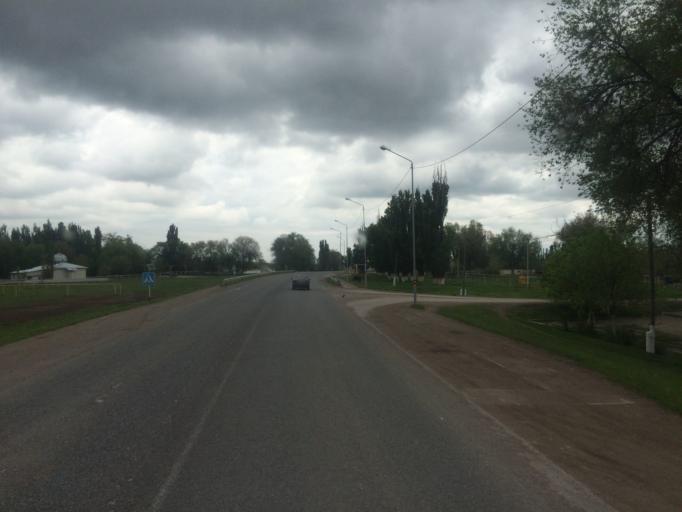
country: KZ
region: Zhambyl
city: Georgiyevka
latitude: 43.1416
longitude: 74.6181
